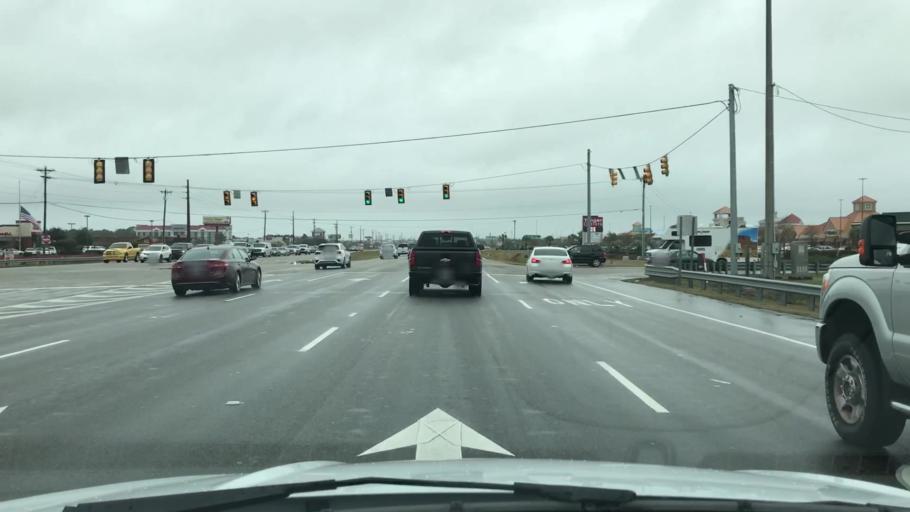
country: US
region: South Carolina
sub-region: Horry County
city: Forestbrook
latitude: 33.7482
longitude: -78.9585
